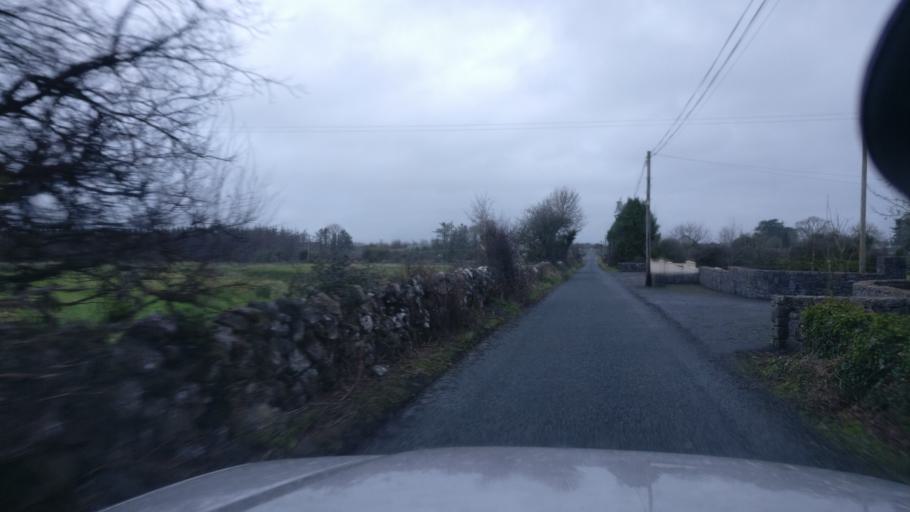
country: IE
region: Connaught
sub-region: County Galway
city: Loughrea
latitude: 53.2153
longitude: -8.6258
